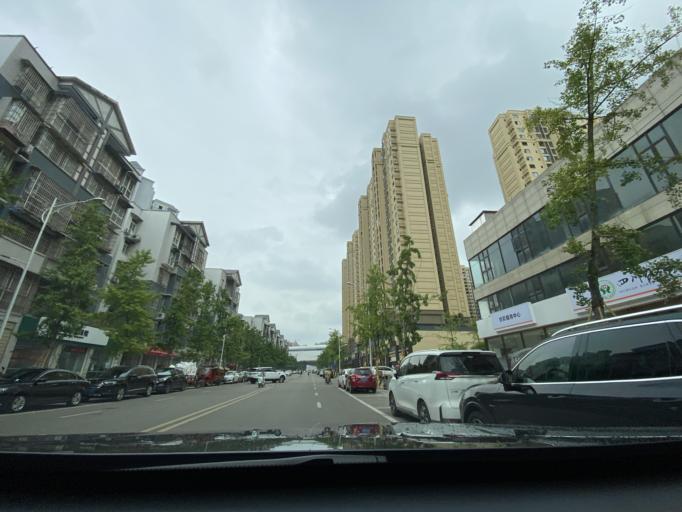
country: CN
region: Sichuan
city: Jiancheng
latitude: 30.4208
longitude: 104.5351
